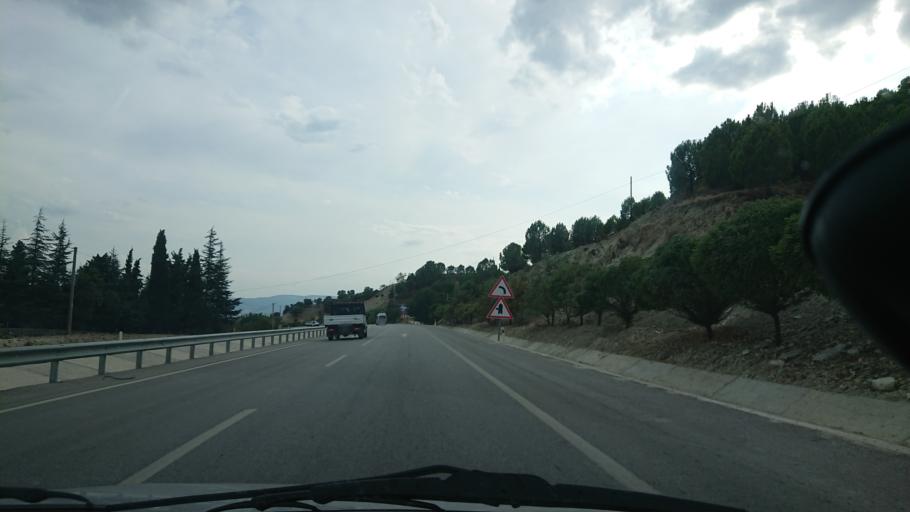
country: TR
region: Kuetahya
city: Gediz
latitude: 39.0246
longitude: 29.4148
